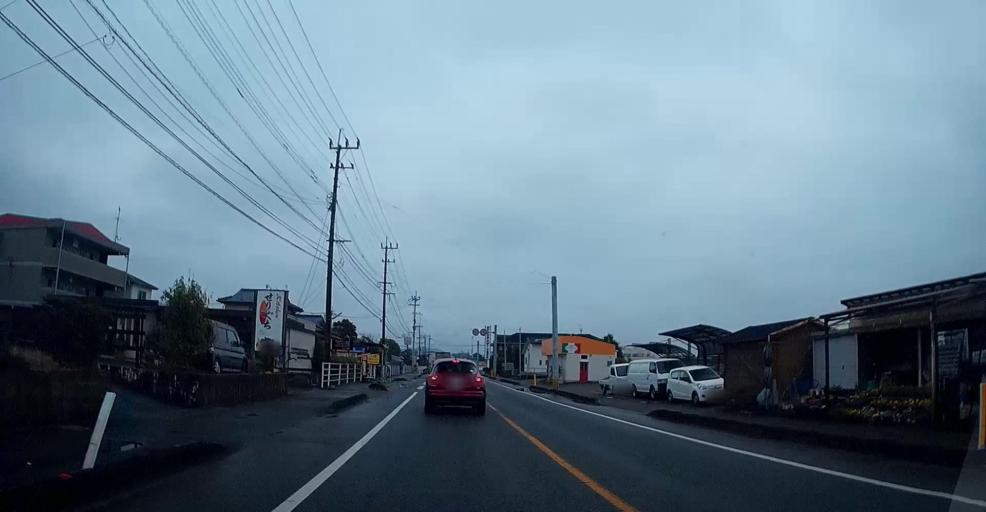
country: JP
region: Kumamoto
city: Kumamoto
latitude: 32.7468
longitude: 130.7385
